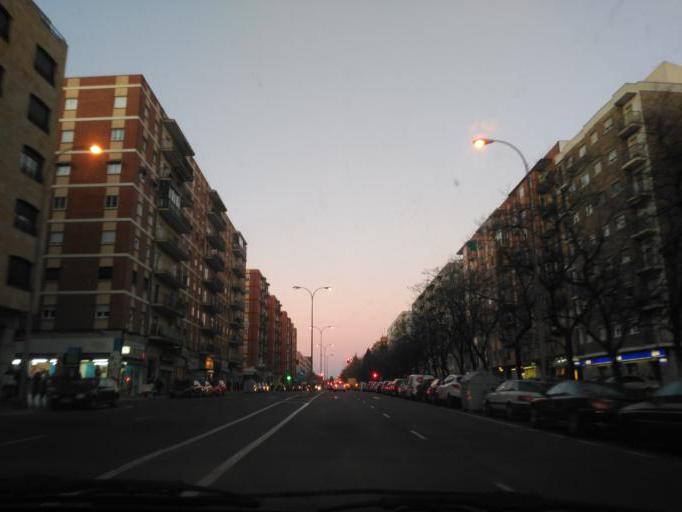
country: ES
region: Castille and Leon
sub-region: Provincia de Salamanca
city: Salamanca
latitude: 40.9752
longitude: -5.6557
